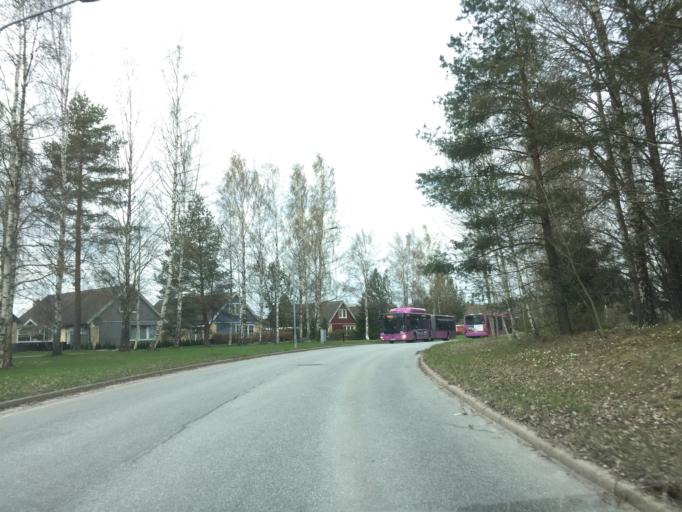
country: SE
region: OErebro
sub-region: Orebro Kommun
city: Orebro
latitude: 59.3112
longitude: 15.1834
